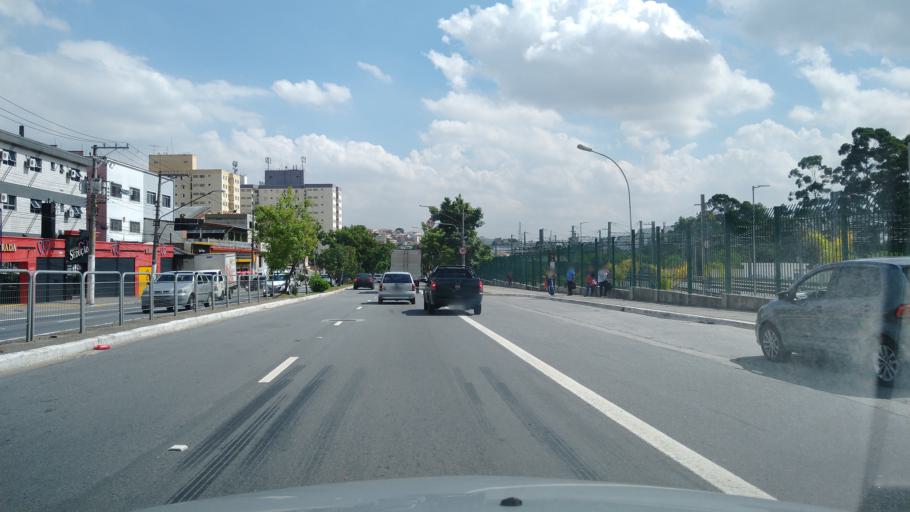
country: BR
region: Sao Paulo
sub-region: Guarulhos
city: Guarulhos
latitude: -23.4988
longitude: -46.5207
